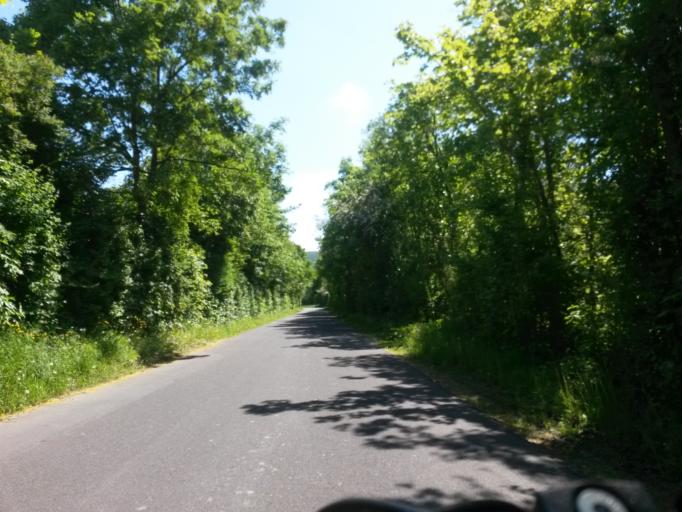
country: DE
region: Bavaria
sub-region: Regierungsbezirk Unterfranken
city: Bad Kissingen
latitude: 50.1844
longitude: 10.0737
